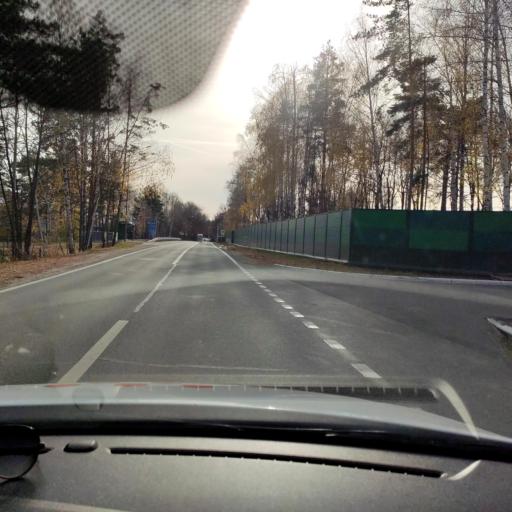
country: RU
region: Tatarstan
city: Verkhniy Uslon
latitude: 55.6267
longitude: 49.0140
